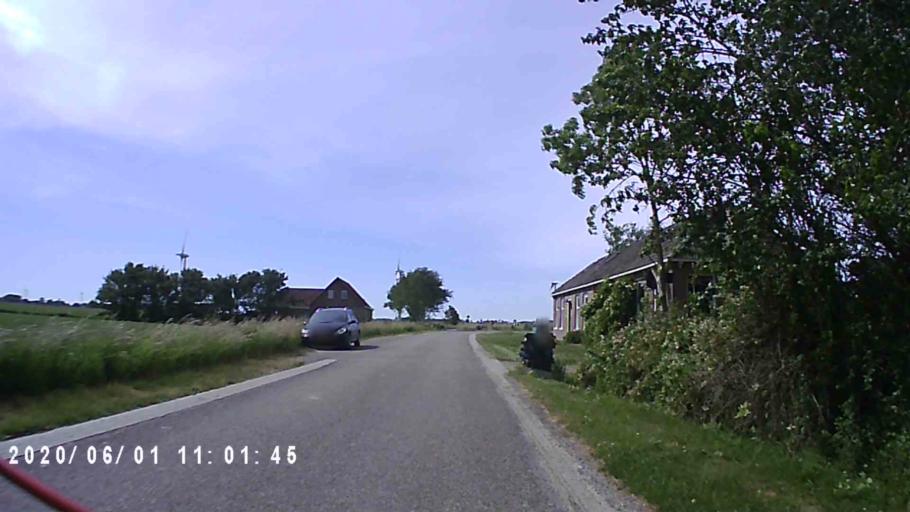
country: NL
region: Friesland
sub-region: Gemeente Franekeradeel
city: Sexbierum
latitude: 53.1959
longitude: 5.4784
